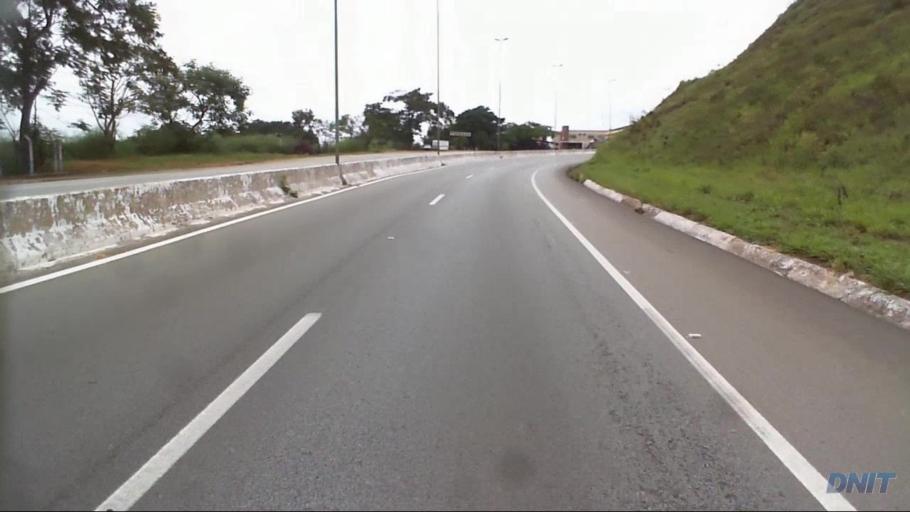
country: BR
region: Minas Gerais
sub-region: Nova Era
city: Nova Era
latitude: -19.7622
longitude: -43.0377
